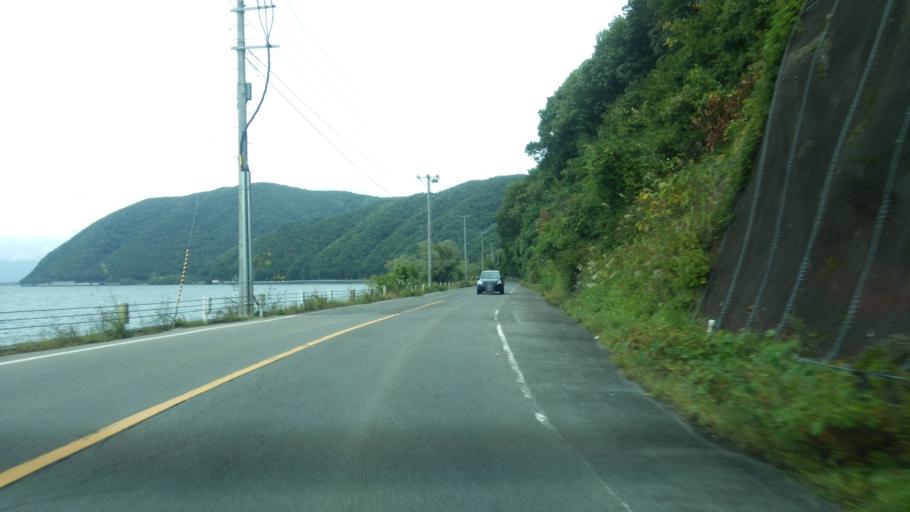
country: JP
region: Fukushima
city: Inawashiro
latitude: 37.4561
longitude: 140.1516
